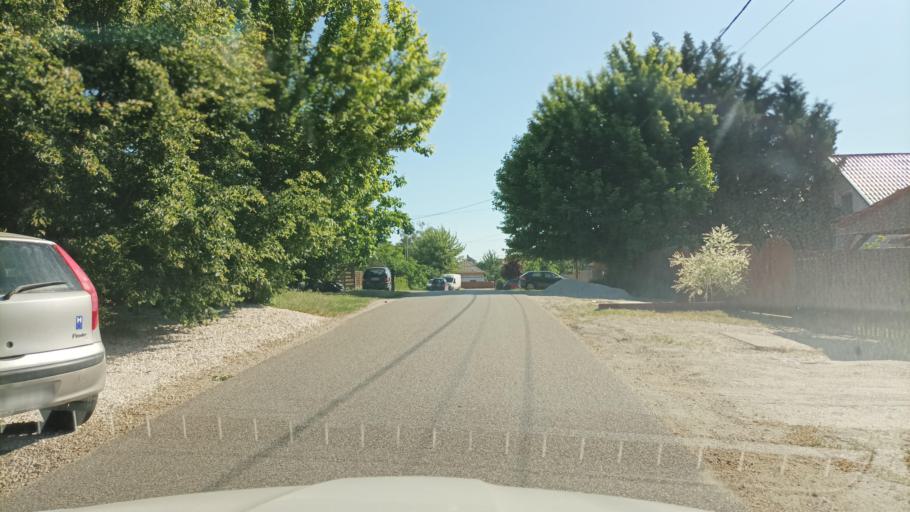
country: HU
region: Pest
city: Szigethalom
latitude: 47.3182
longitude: 19.0145
